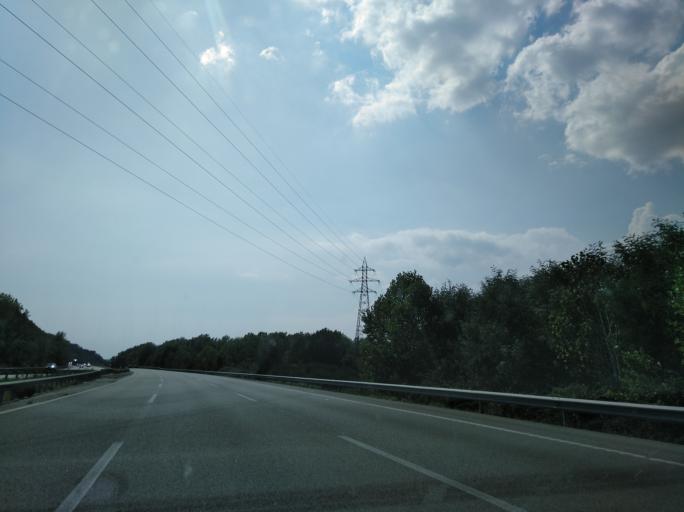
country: ES
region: Catalonia
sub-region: Provincia de Girona
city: Breda
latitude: 41.7119
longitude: 2.5375
